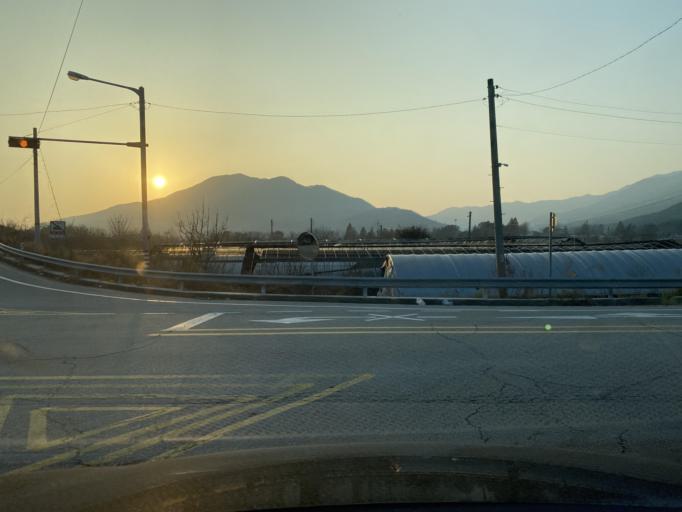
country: KR
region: Chungcheongnam-do
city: Hongsung
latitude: 36.6840
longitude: 126.6590
